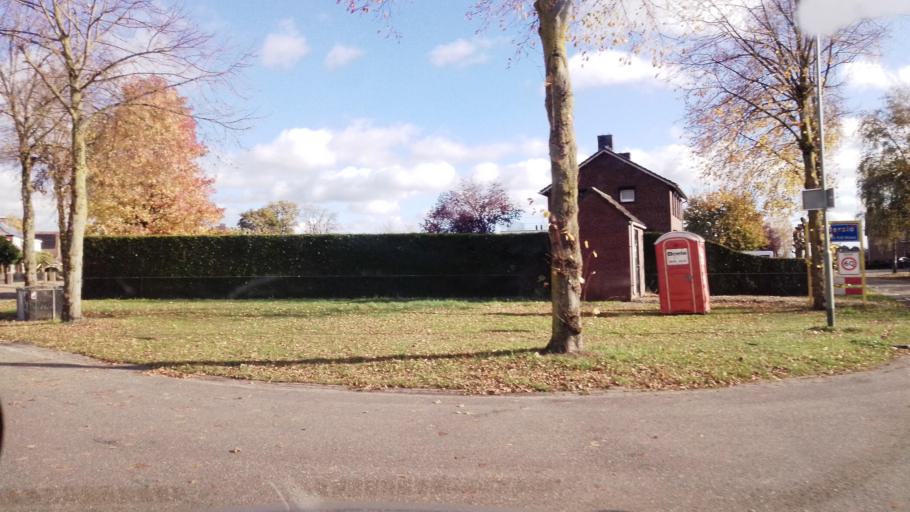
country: NL
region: Limburg
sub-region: Gemeente Bergen
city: Wellerlooi
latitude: 51.4583
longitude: 6.0858
